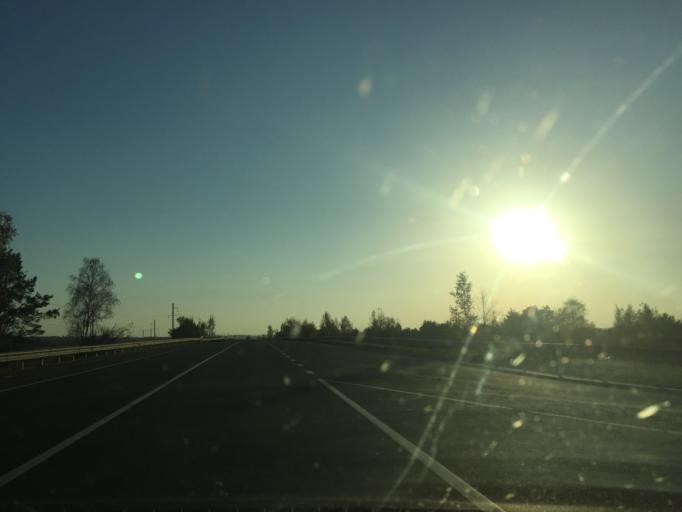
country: BY
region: Mogilev
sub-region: Mahilyowski Rayon
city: Veyno
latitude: 53.8137
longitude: 30.4590
